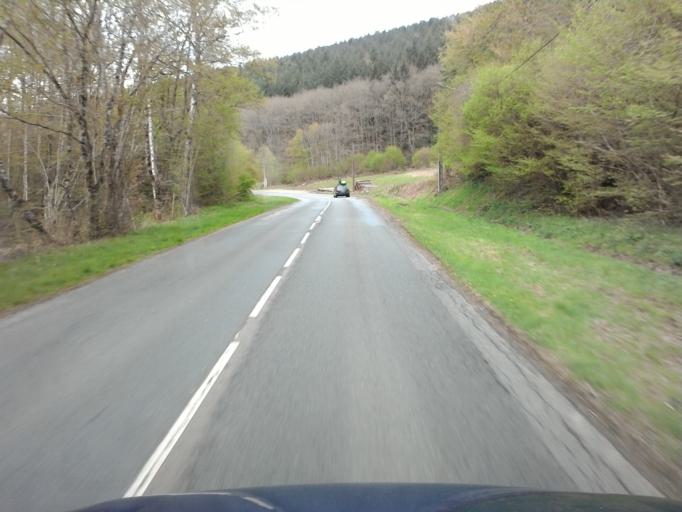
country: FR
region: Bourgogne
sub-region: Departement de la Cote-d'Or
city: Saulieu
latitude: 47.2997
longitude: 4.0341
